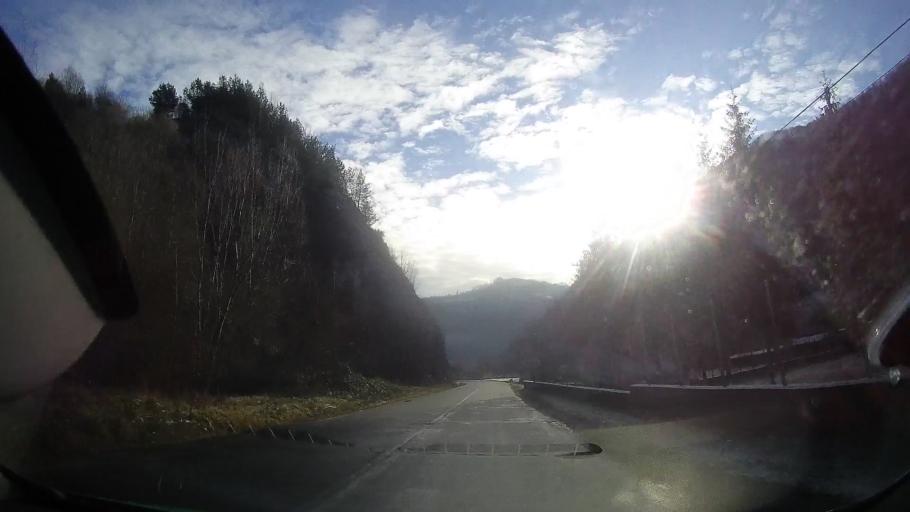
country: RO
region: Alba
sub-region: Comuna Sohodol
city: Sohodol
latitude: 46.3590
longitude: 23.0226
